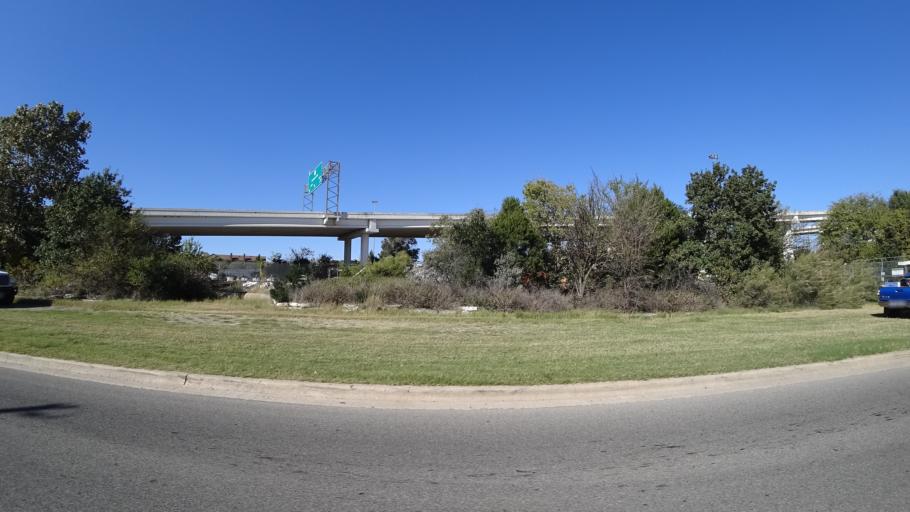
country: US
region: Texas
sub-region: Williamson County
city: Jollyville
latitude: 30.3768
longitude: -97.7381
